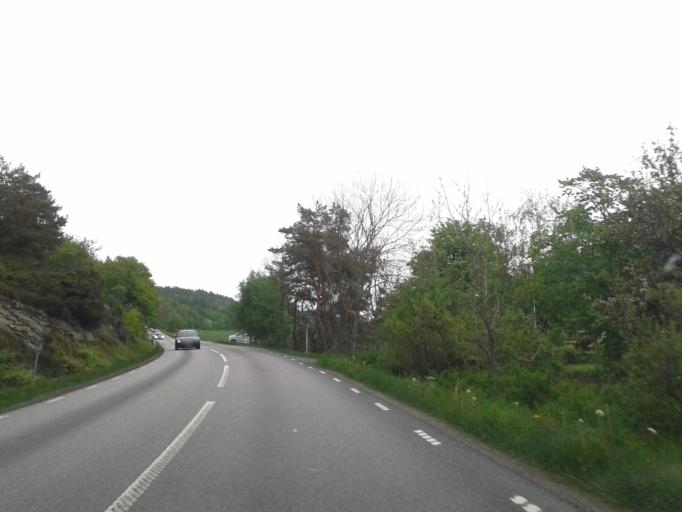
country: SE
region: Vaestra Goetaland
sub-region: Kungalvs Kommun
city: Kode
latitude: 57.8907
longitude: 11.7490
